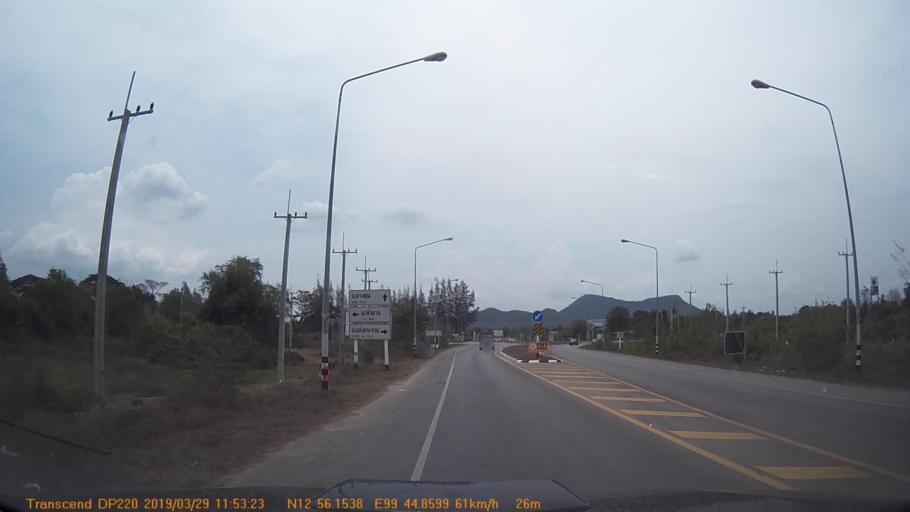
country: TH
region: Phetchaburi
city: Kaeng Krachan
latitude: 12.9357
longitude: 99.7477
